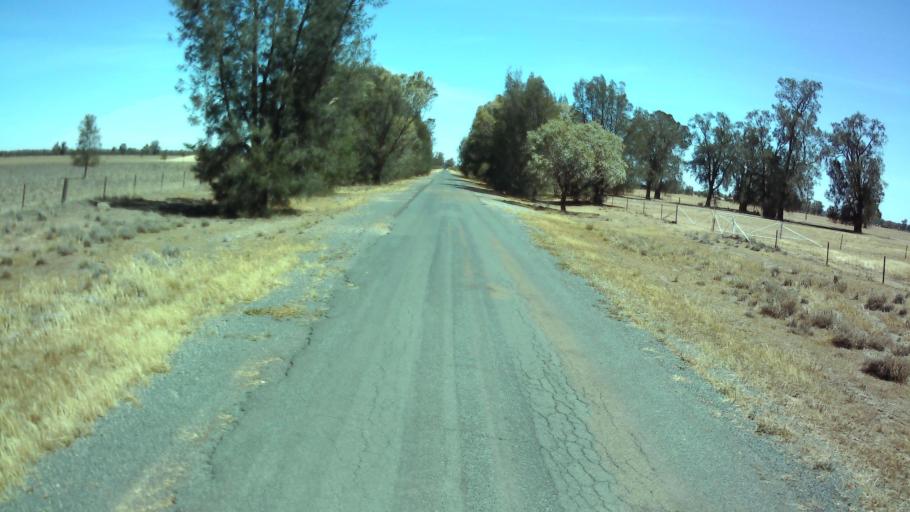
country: AU
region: New South Wales
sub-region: Weddin
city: Grenfell
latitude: -33.8874
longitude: 147.6889
